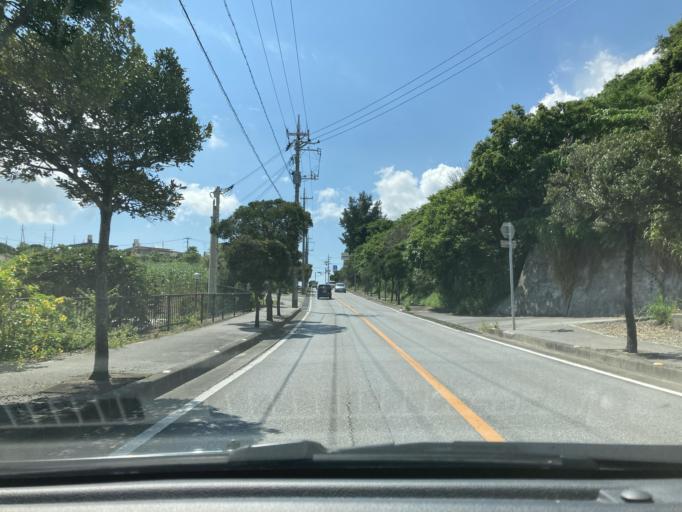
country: JP
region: Okinawa
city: Tomigusuku
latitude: 26.1677
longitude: 127.7544
